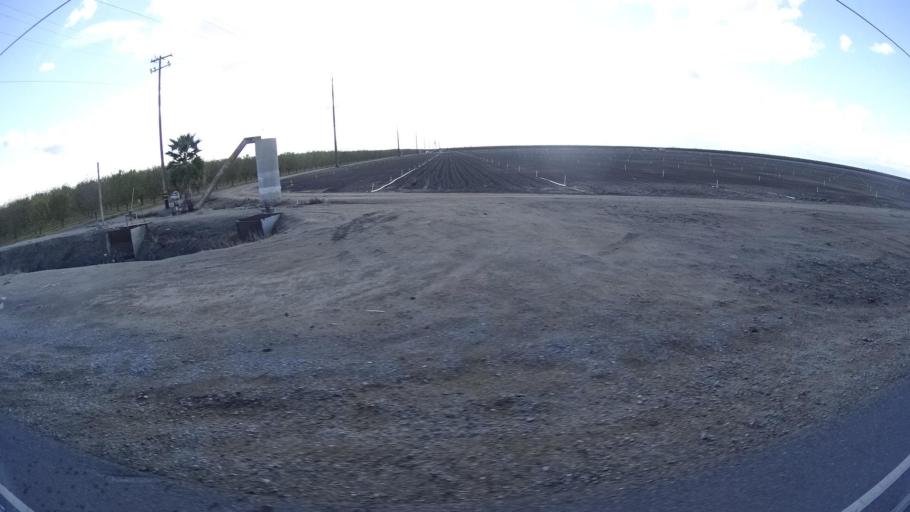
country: US
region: California
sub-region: Kern County
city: Greenfield
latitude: 35.2671
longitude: -119.0970
